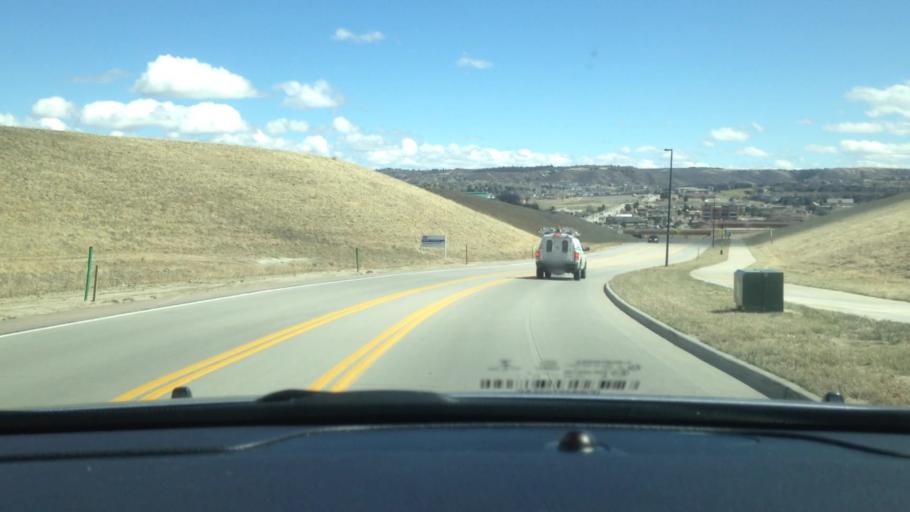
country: US
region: Colorado
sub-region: Douglas County
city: Castle Rock
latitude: 39.3692
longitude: -104.8726
